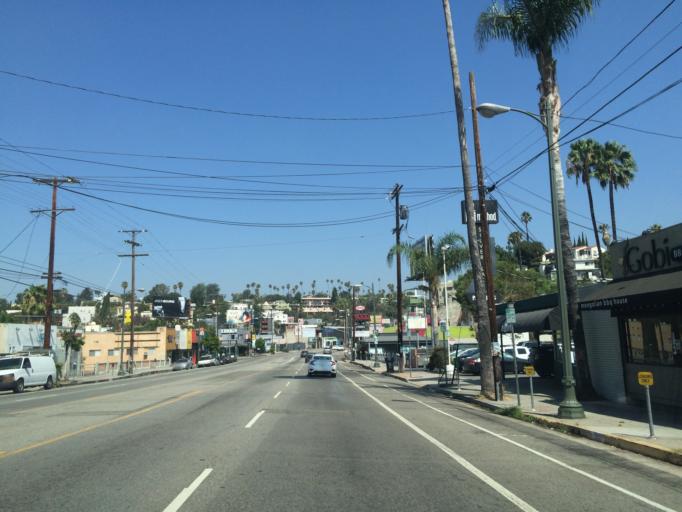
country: US
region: California
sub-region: Los Angeles County
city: Silver Lake
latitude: 34.0822
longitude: -118.2722
